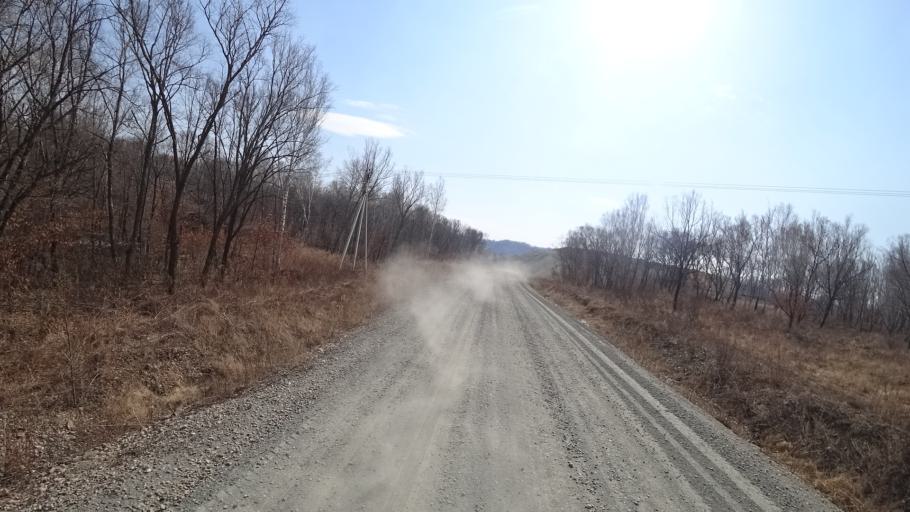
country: RU
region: Amur
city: Novobureyskiy
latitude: 49.8007
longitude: 129.9599
